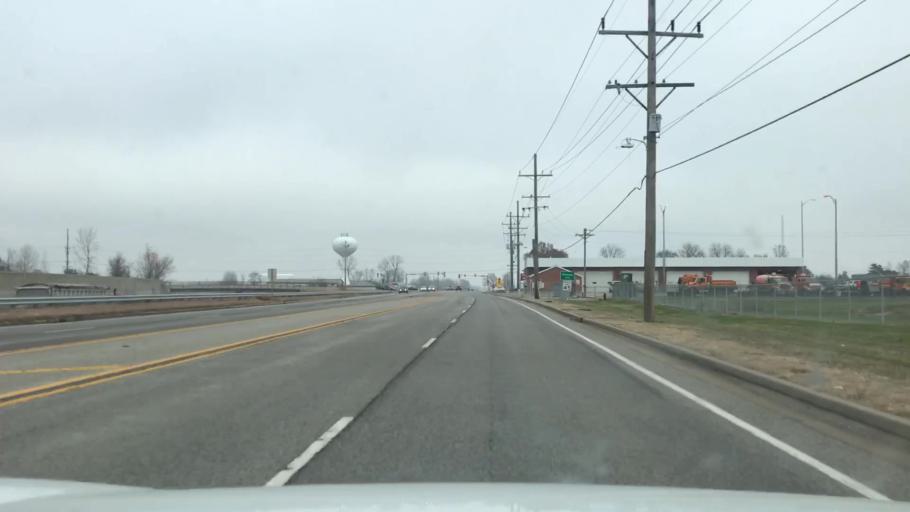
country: US
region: Illinois
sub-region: Madison County
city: Rosewood Heights
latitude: 38.8847
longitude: -90.0589
